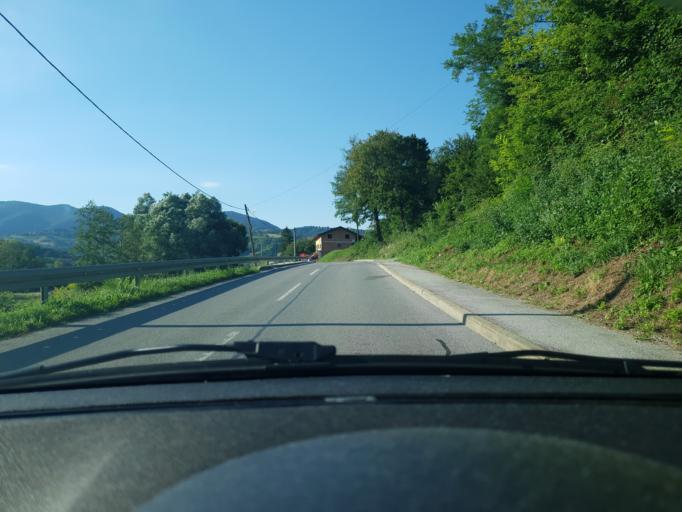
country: HR
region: Krapinsko-Zagorska
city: Radoboj
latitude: 46.1508
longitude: 15.9425
